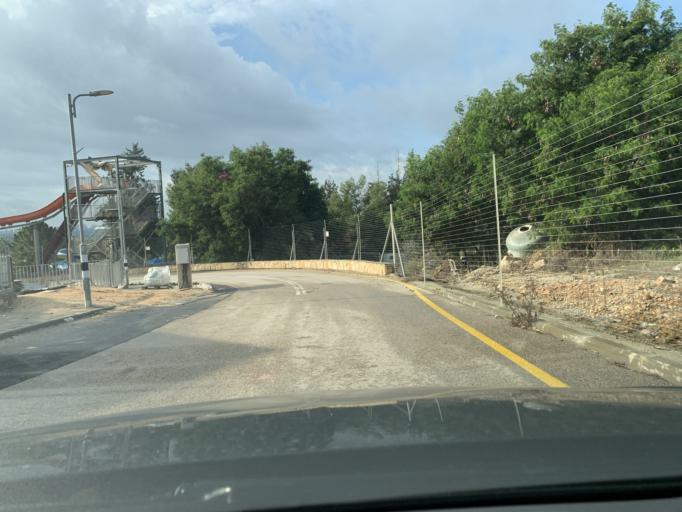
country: IL
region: Central District
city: Rosh Ha'Ayin
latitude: 32.0640
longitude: 34.9497
